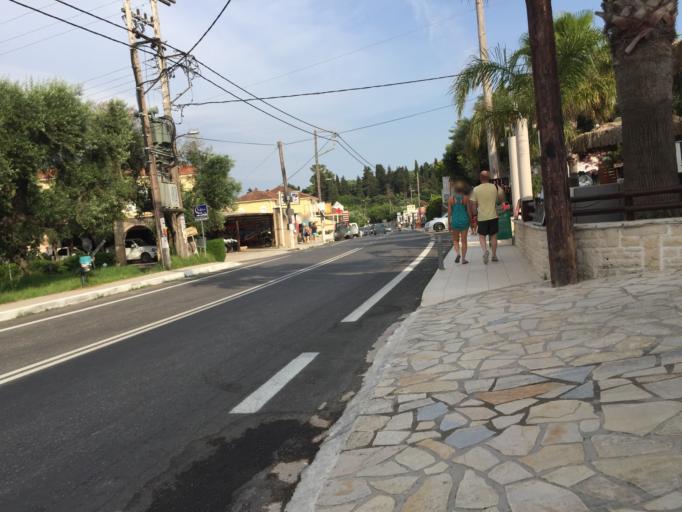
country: GR
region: Ionian Islands
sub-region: Nomos Zakynthou
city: Gaitanion
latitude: 37.8144
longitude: 20.8666
